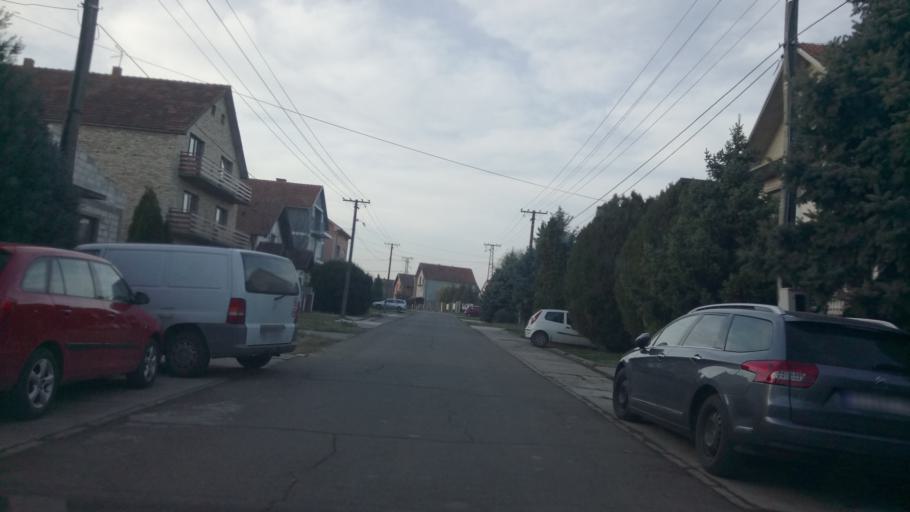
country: RS
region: Autonomna Pokrajina Vojvodina
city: Nova Pazova
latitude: 44.9336
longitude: 20.2192
